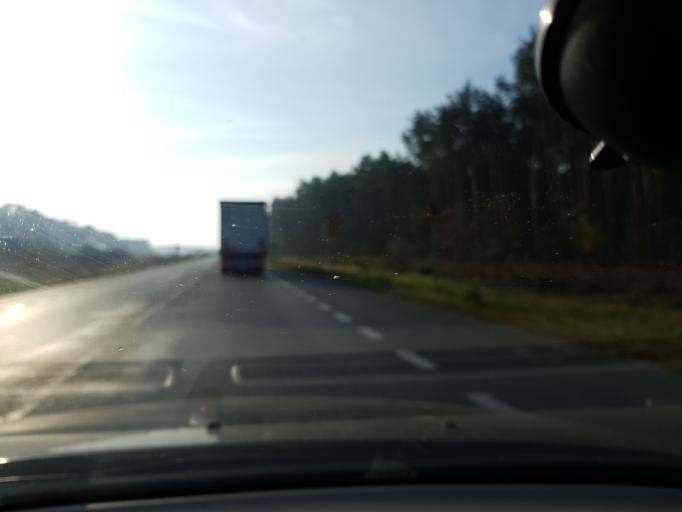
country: PL
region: Masovian Voivodeship
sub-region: Powiat otwocki
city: Otwock
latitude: 52.1569
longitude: 21.3089
